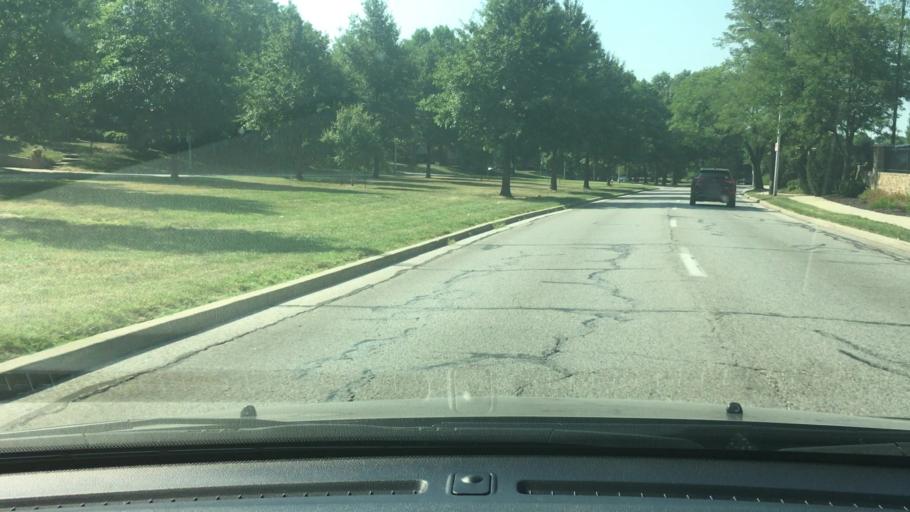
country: US
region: Kansas
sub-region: Johnson County
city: Leawood
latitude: 38.9718
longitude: -94.6055
